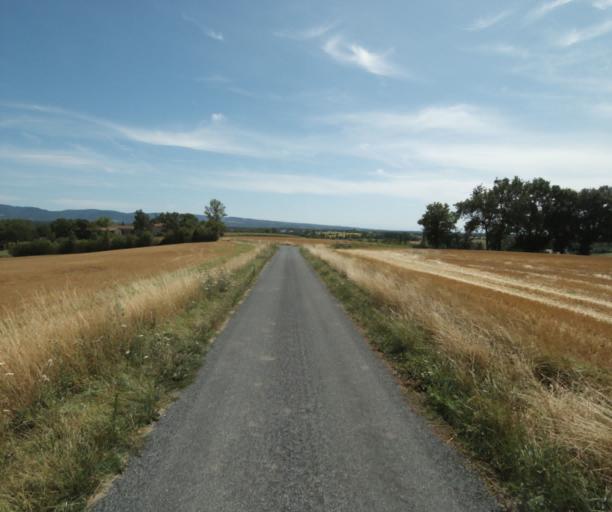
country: FR
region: Midi-Pyrenees
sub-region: Departement du Tarn
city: Puylaurens
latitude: 43.5302
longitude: 2.0030
